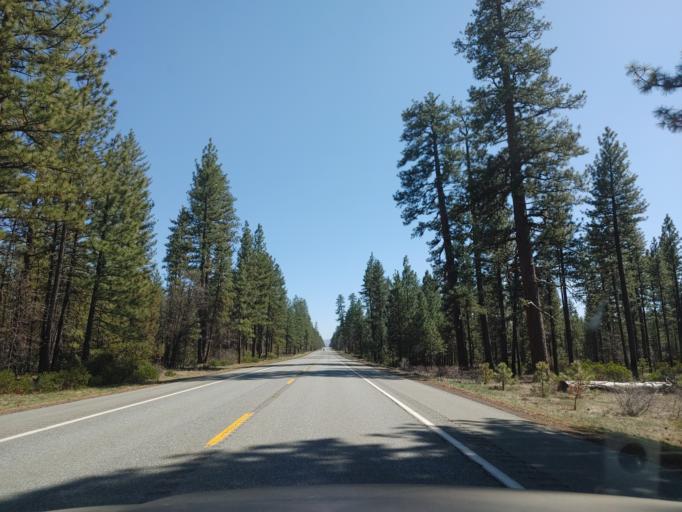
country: US
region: California
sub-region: Shasta County
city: Burney
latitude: 40.9811
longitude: -121.6234
